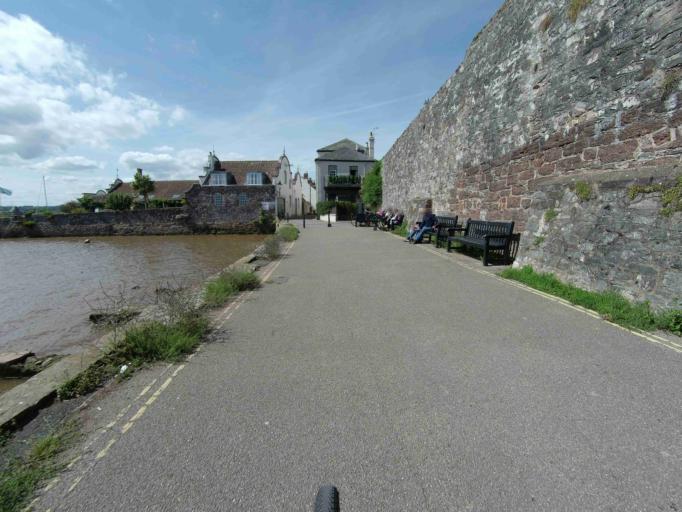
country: GB
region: England
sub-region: Devon
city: Topsham
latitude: 50.6826
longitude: -3.4662
